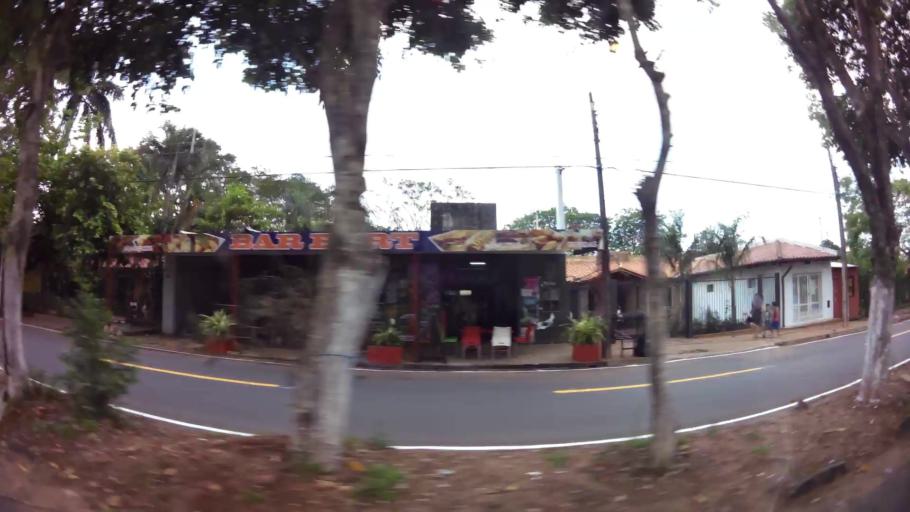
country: PY
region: Central
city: Nemby
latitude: -25.3682
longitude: -57.5575
